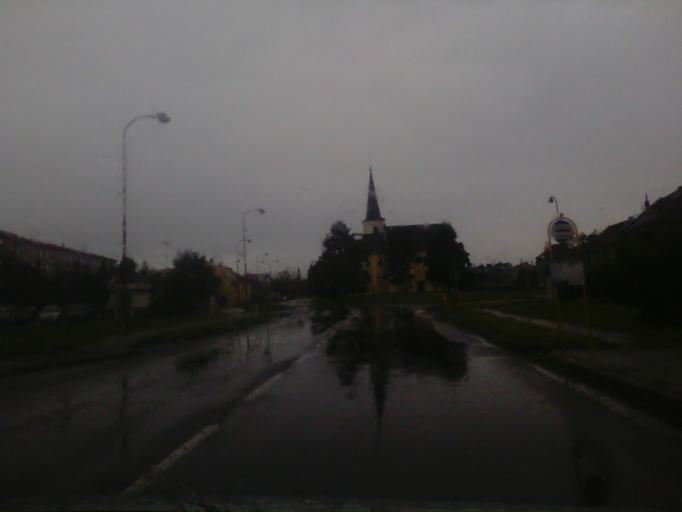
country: CZ
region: Olomoucky
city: Litovel
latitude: 49.7091
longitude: 17.0742
